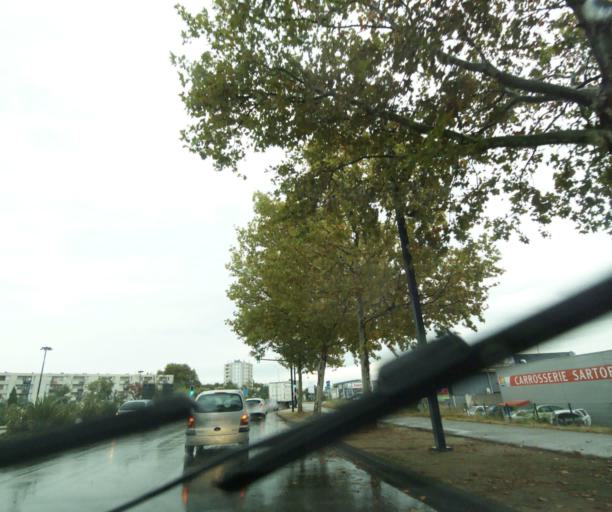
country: FR
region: Languedoc-Roussillon
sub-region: Departement du Gard
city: Nimes
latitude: 43.8408
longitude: 4.3897
